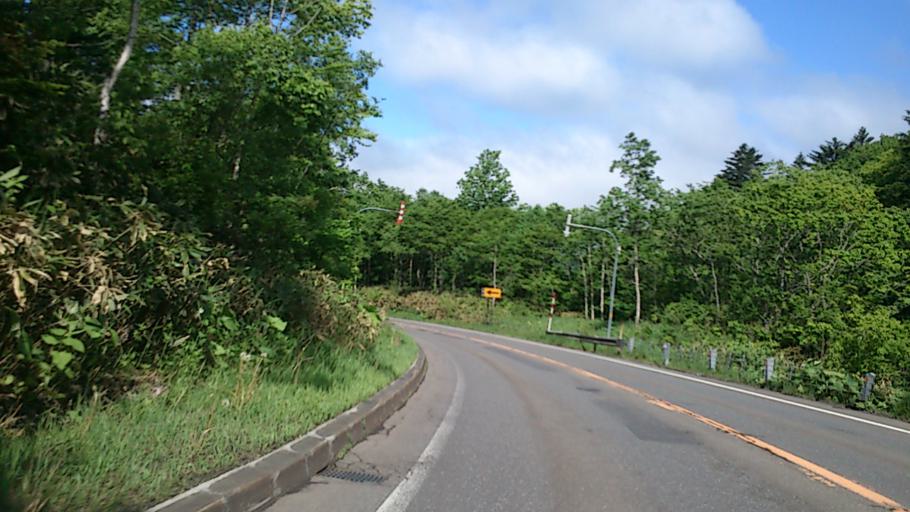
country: JP
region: Hokkaido
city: Shiraoi
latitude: 42.7177
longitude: 141.2233
